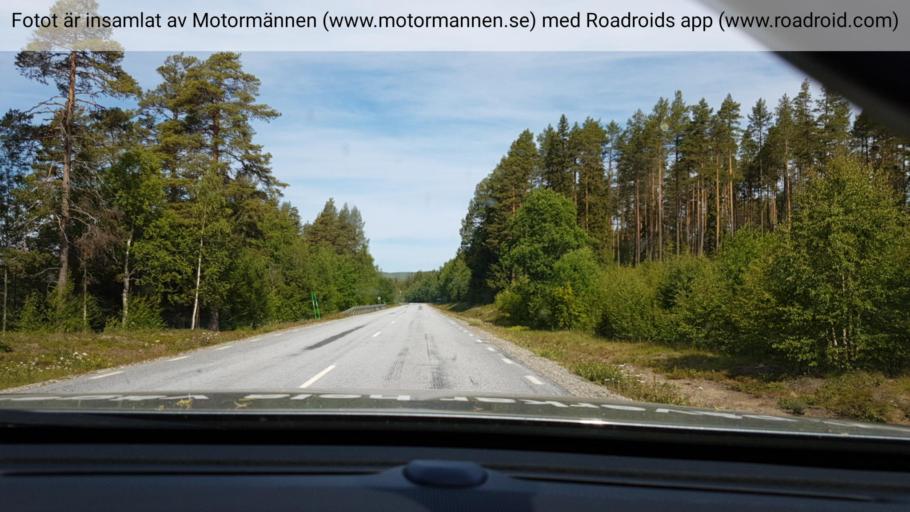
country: SE
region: Vaesterbotten
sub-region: Asele Kommun
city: Asele
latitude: 64.1808
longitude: 17.2759
